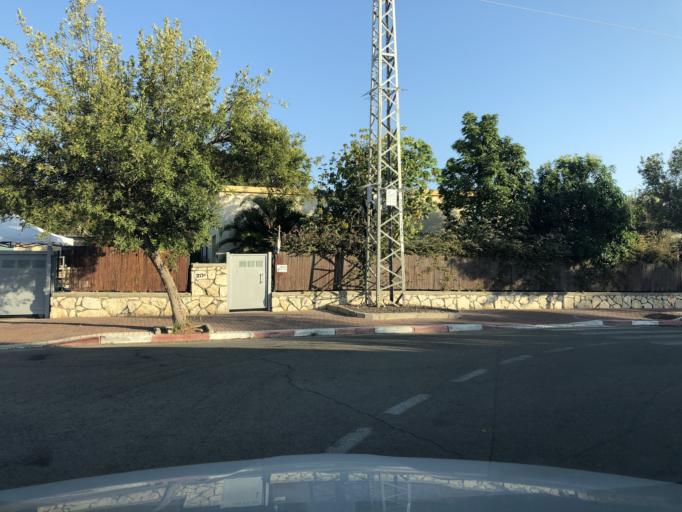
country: PS
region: West Bank
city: Hablah
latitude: 32.1614
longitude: 34.9697
